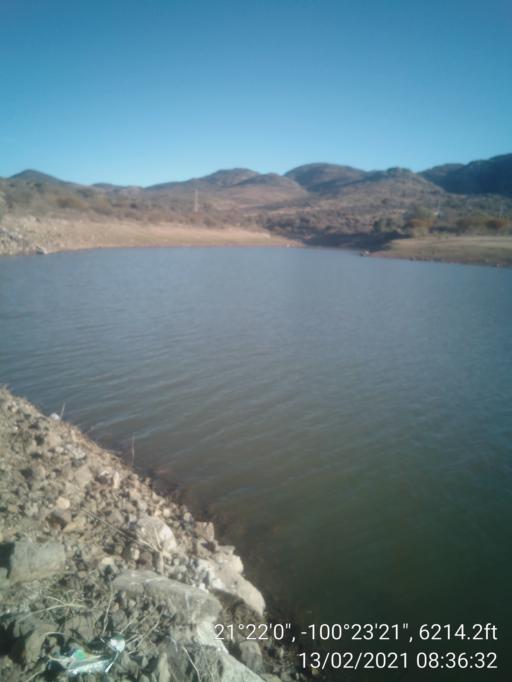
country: MX
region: Guanajuato
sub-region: San Luis de la Paz
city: San Luis de la Paz
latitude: 21.3667
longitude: -100.3893
